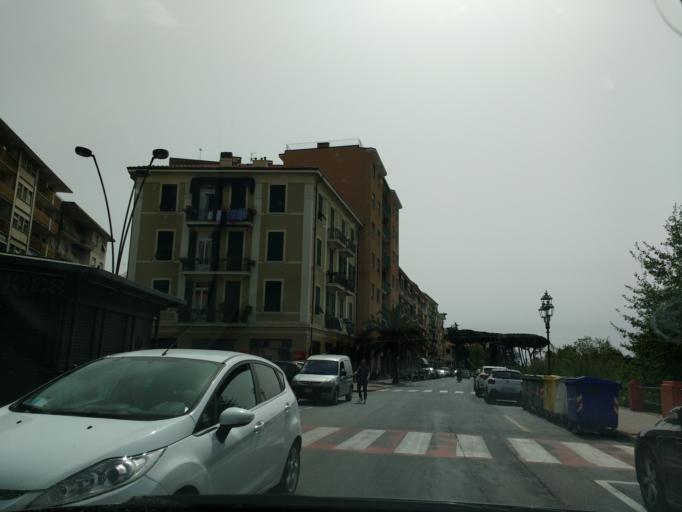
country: IT
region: Liguria
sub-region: Provincia di Imperia
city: Ventimiglia
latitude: 43.7919
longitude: 7.6059
